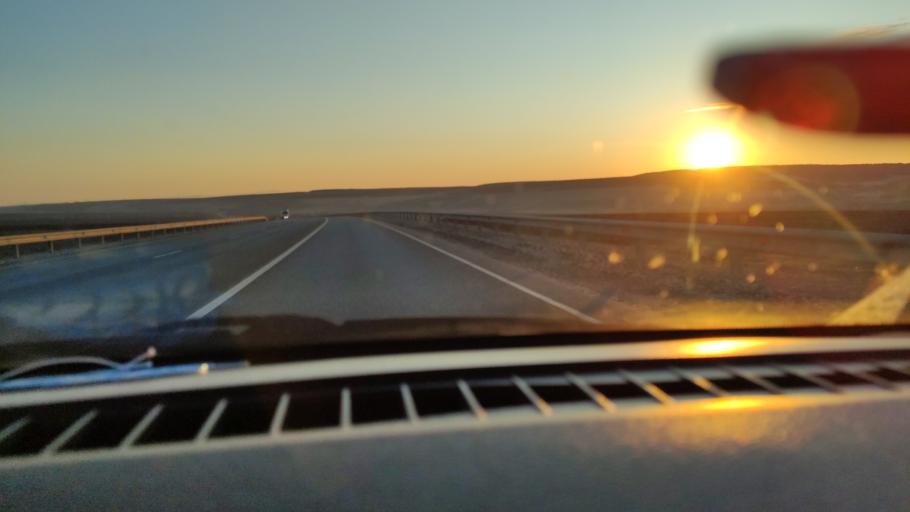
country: RU
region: Saratov
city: Yelshanka
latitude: 51.8370
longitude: 46.4733
